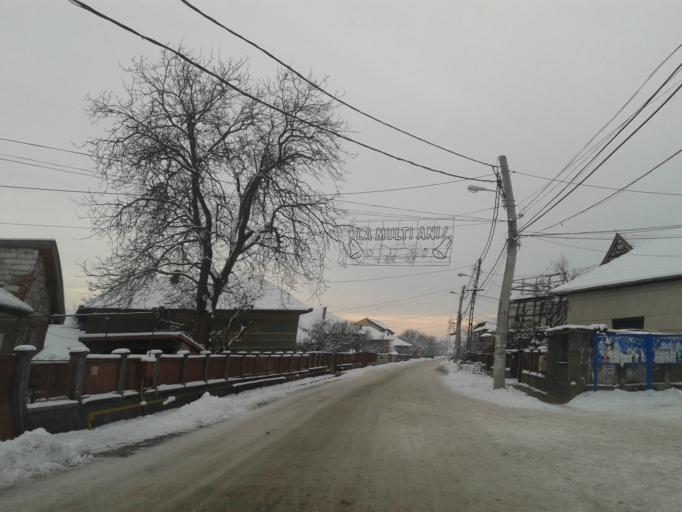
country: RO
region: Hunedoara
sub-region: Municipiul Deva
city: Cristur
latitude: 45.8244
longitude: 22.9415
